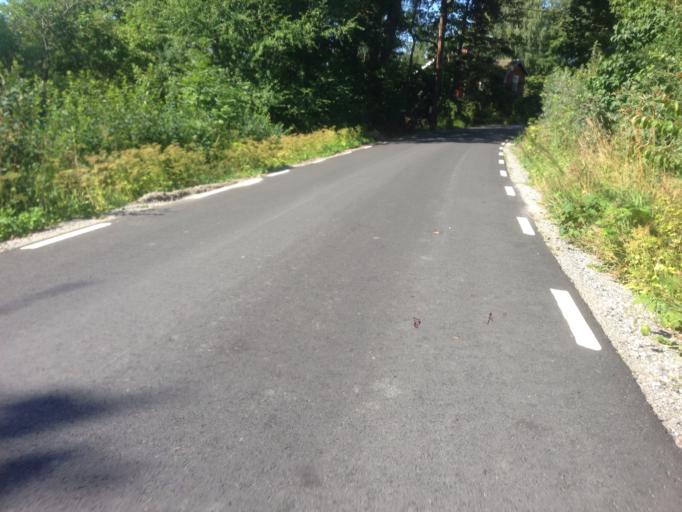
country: SE
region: Stockholm
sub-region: Vaxholms Kommun
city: Vaxholm
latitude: 59.3766
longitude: 18.3901
